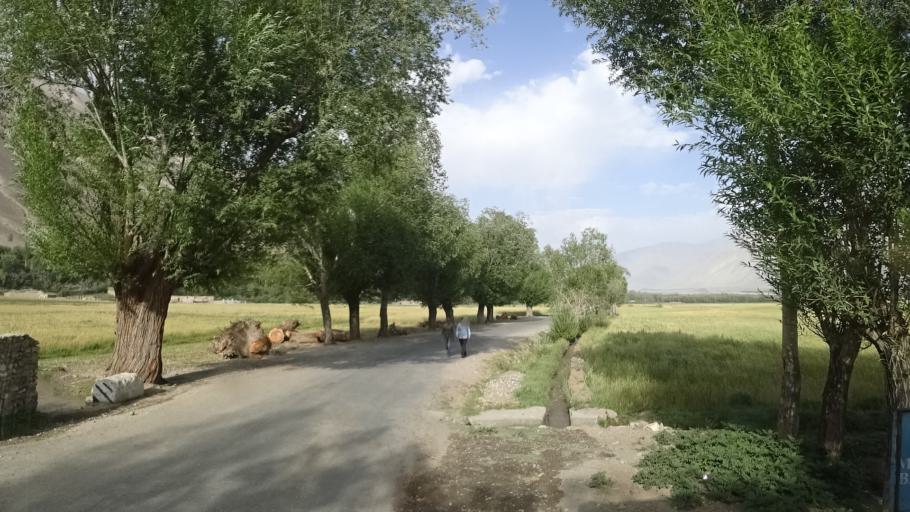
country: AF
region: Badakhshan
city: Khandud
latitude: 37.0049
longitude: 72.3761
